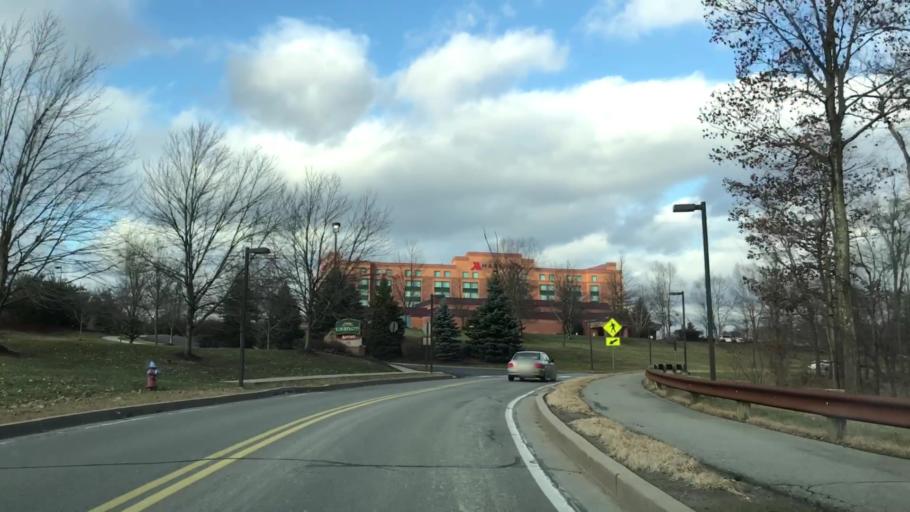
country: US
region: Pennsylvania
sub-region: Butler County
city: Cranberry Township
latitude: 40.6827
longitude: -80.0905
